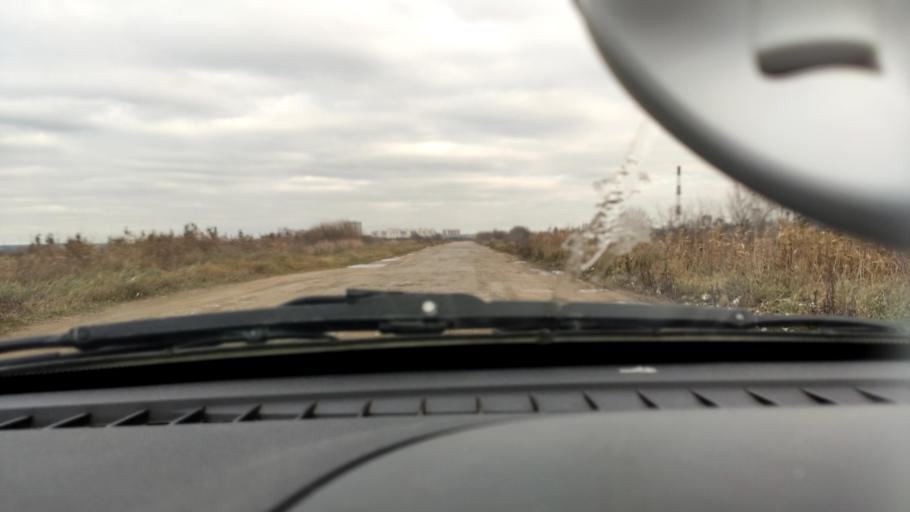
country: RU
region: Perm
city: Kondratovo
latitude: 57.9886
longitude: 56.0881
